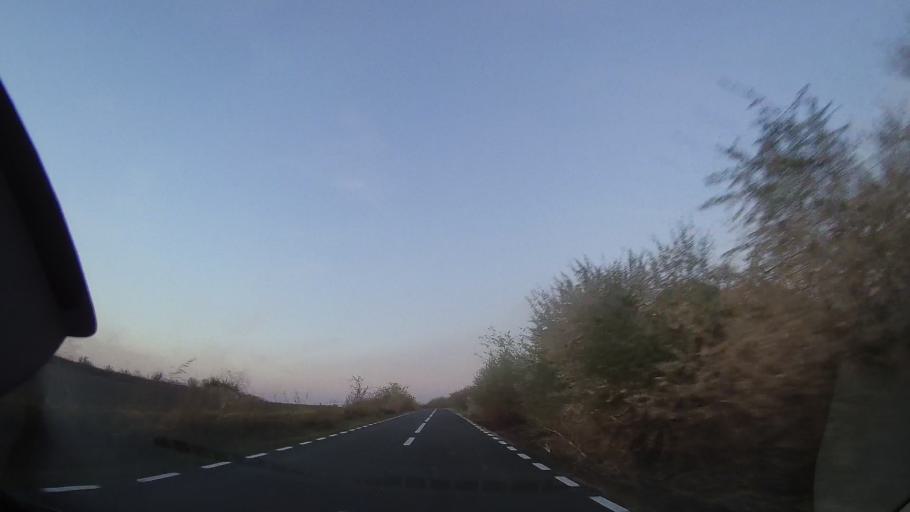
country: RO
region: Constanta
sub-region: Comuna Cobadin
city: Cobadin
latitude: 44.0336
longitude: 28.2603
